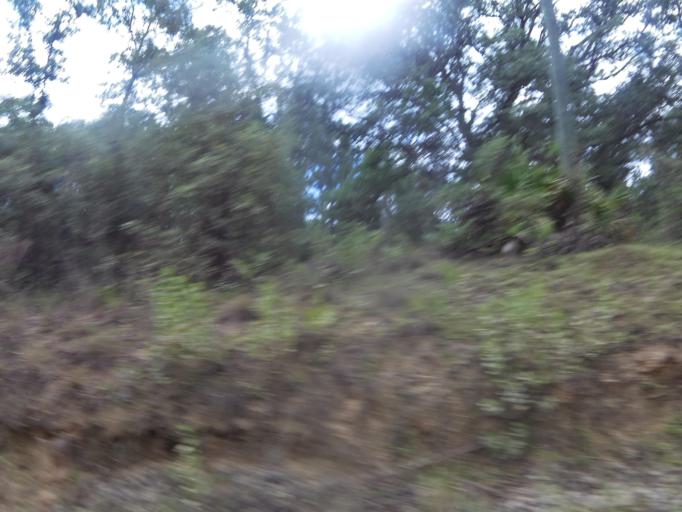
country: US
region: Florida
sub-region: Clay County
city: Asbury Lake
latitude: 29.9104
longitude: -81.7960
